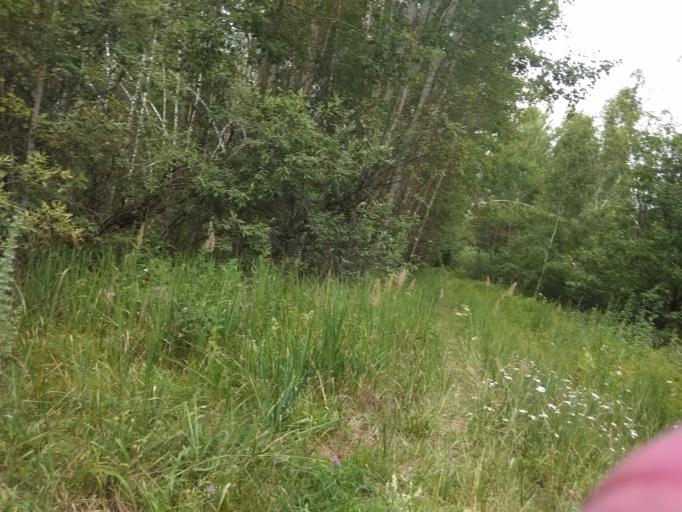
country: RU
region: Moskovskaya
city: Misheronskiy
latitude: 55.6493
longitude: 39.6918
